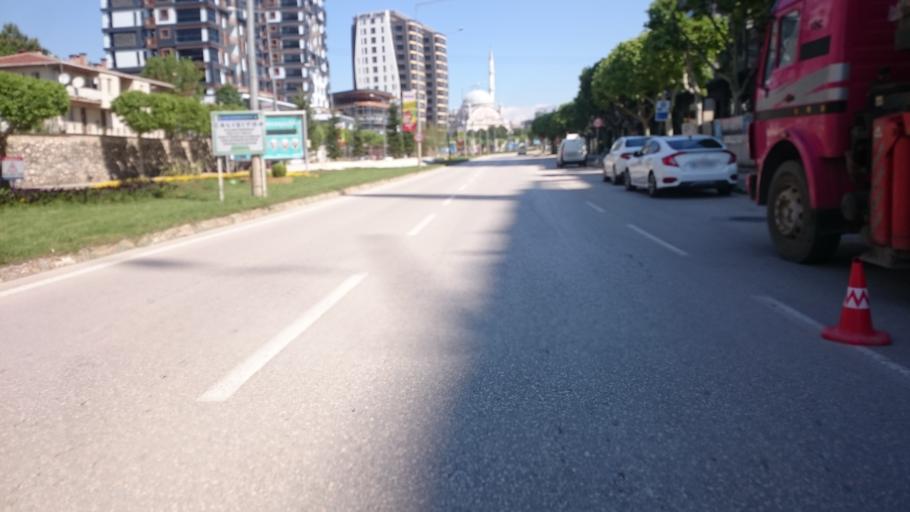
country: TR
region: Bursa
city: Yildirim
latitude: 40.2137
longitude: 28.9772
